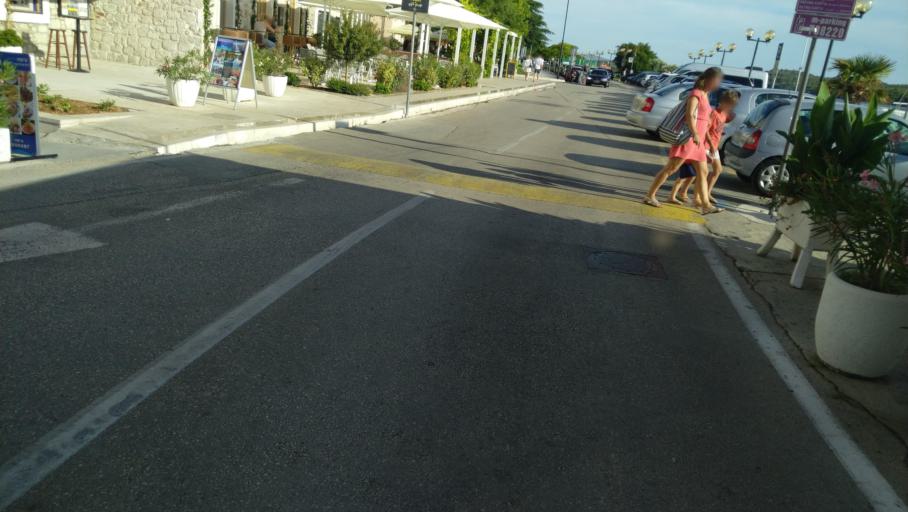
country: HR
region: Sibensko-Kniniska
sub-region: Grad Sibenik
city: Sibenik
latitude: 43.7369
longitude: 15.8879
